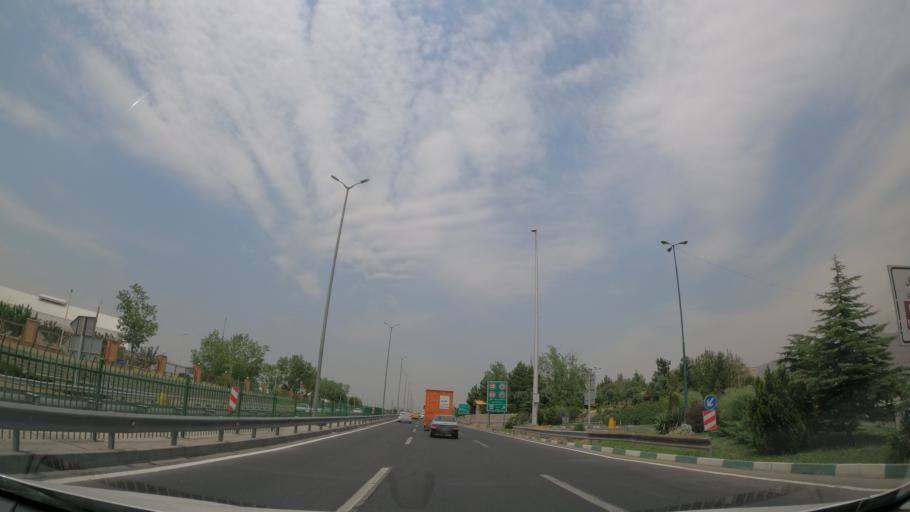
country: IR
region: Tehran
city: Shahr-e Qods
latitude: 35.7389
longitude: 51.2602
